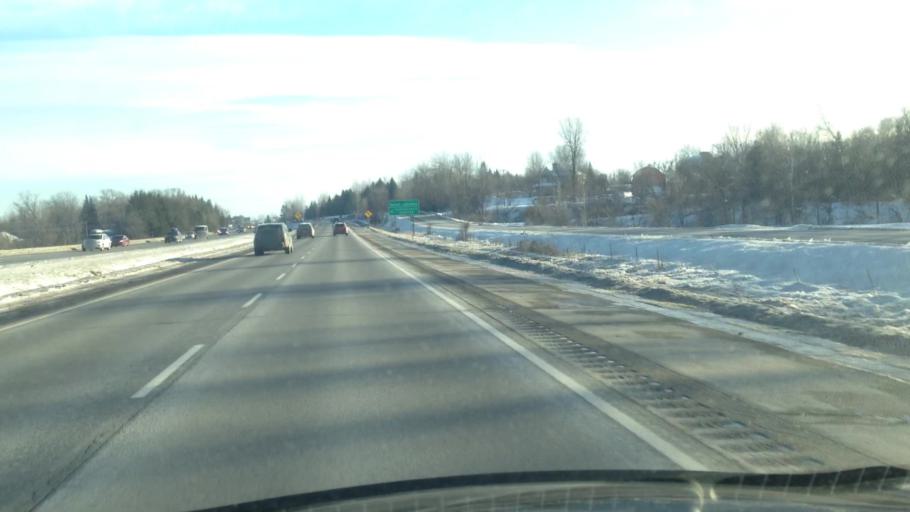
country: CA
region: Quebec
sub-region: Laurentides
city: Prevost
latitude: 45.8174
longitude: -74.0522
